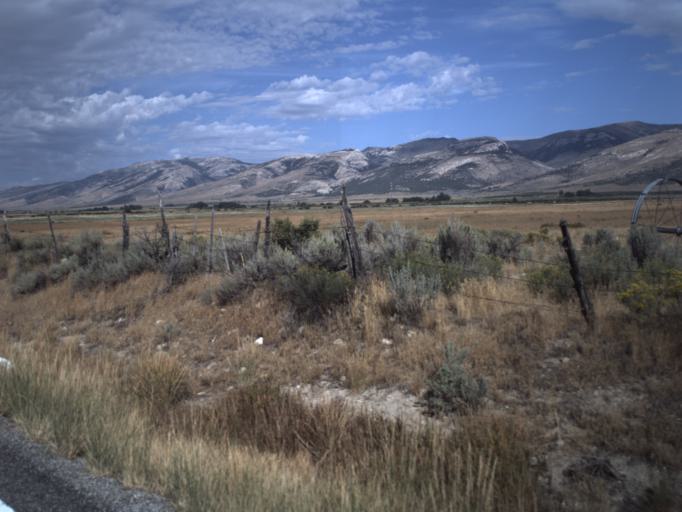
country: US
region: Idaho
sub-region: Cassia County
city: Burley
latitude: 41.8171
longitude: -113.3066
